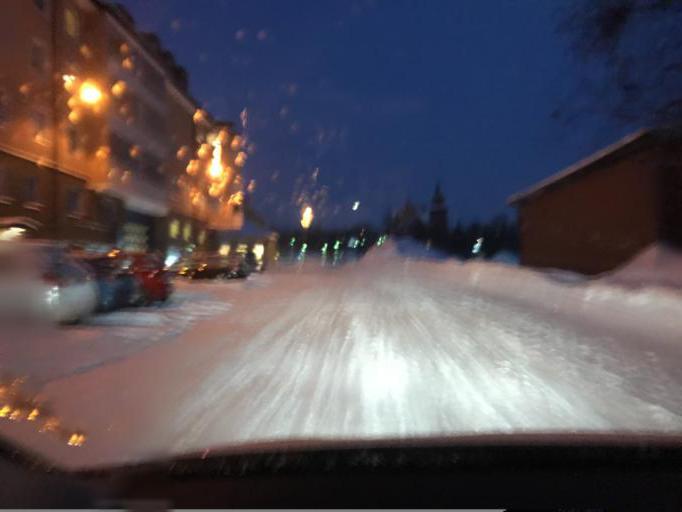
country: SE
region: Norrbotten
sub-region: Kiruna Kommun
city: Kiruna
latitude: 67.8530
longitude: 20.2261
